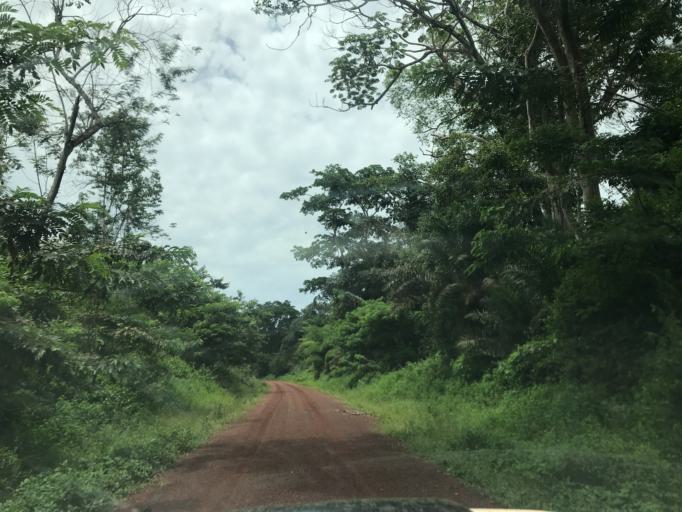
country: CD
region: Eastern Province
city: Buta
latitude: 2.3636
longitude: 24.9435
